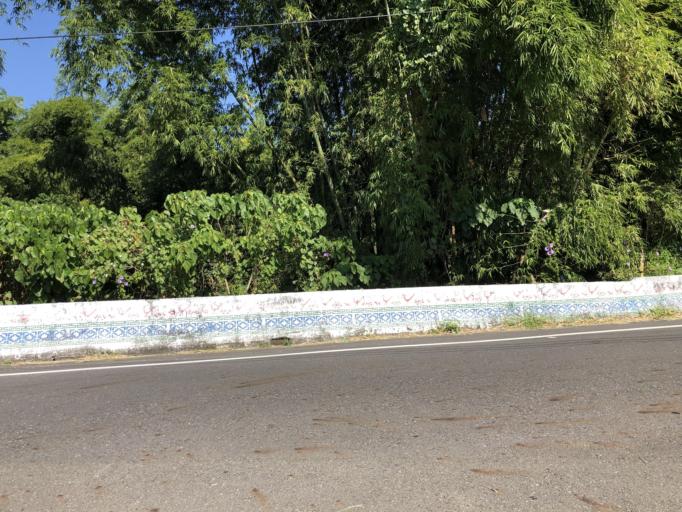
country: TW
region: Taiwan
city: Yujing
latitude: 23.0555
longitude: 120.4020
